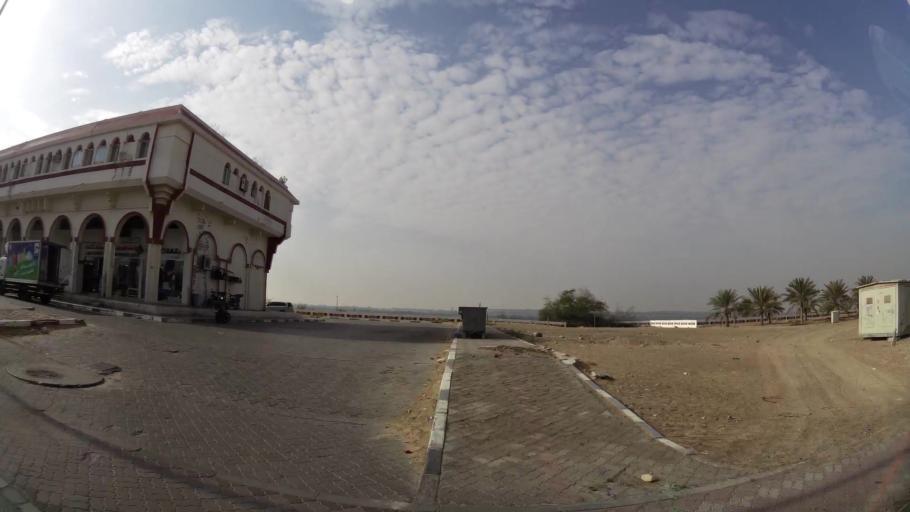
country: AE
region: Abu Dhabi
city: Abu Dhabi
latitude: 24.2399
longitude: 54.7173
